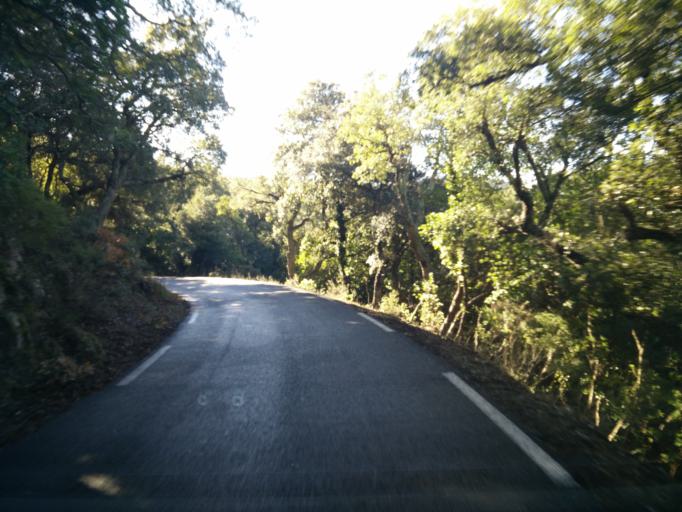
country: FR
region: Provence-Alpes-Cote d'Azur
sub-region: Departement du Var
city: Collobrieres
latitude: 43.2417
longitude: 6.3576
